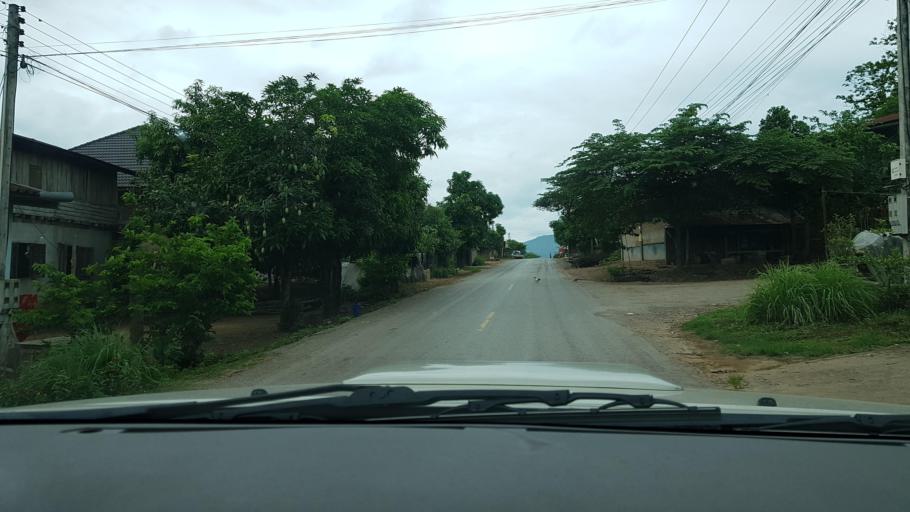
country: LA
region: Loungnamtha
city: Muang Nale
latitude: 20.2884
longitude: 101.6265
